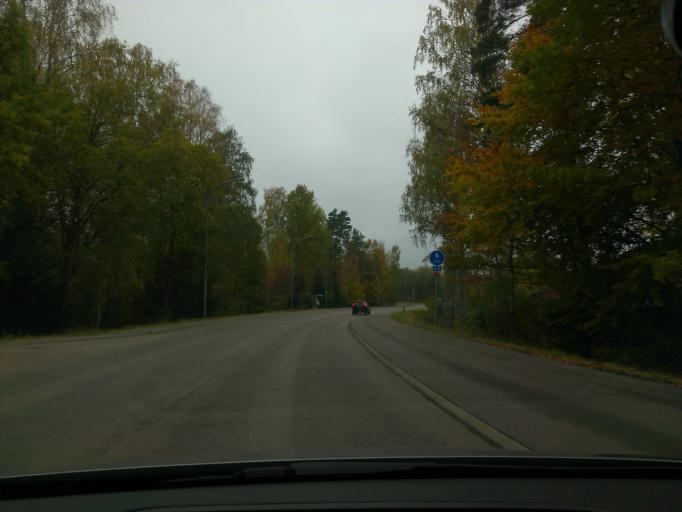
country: SE
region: Kronoberg
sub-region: Vaxjo Kommun
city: Vaexjoe
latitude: 56.8929
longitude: 14.7391
